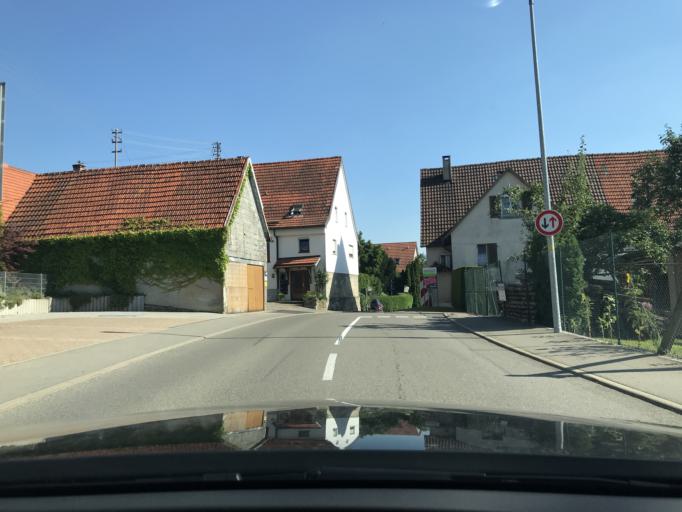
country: DE
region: Baden-Wuerttemberg
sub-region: Regierungsbezirk Stuttgart
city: Winterbach
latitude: 48.7746
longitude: 9.5024
